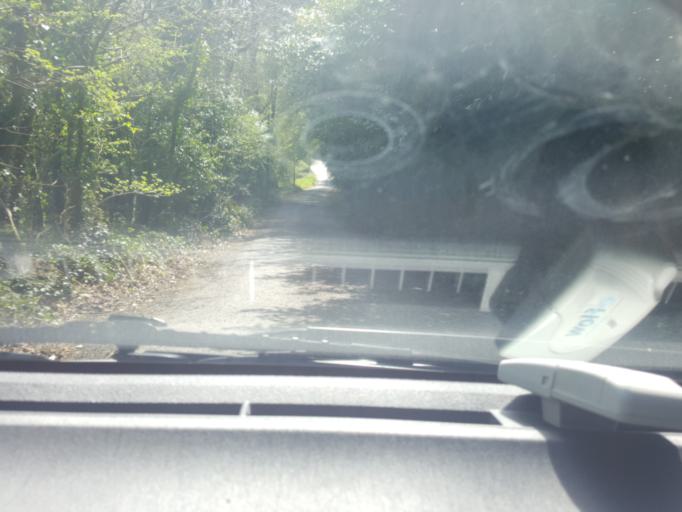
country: IE
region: Munster
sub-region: County Cork
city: Bandon
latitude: 51.7691
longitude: -8.6763
